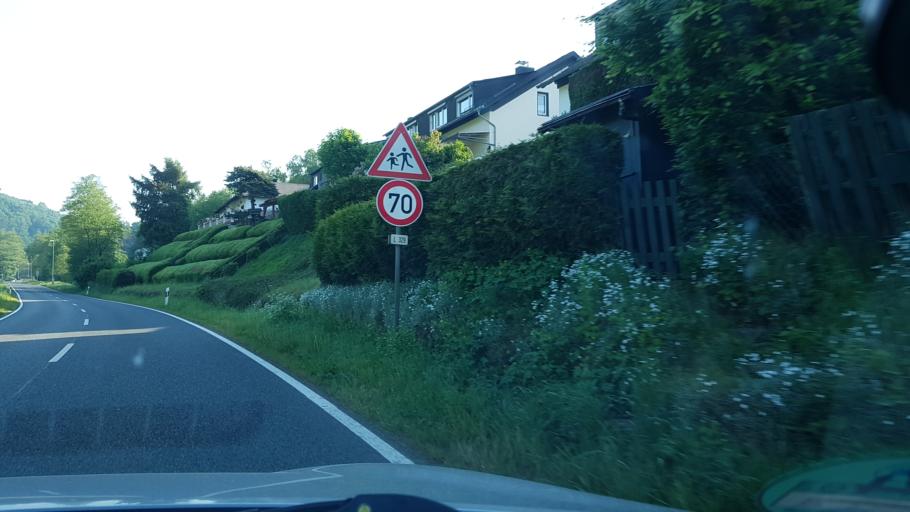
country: DE
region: Rheinland-Pfalz
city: Eitelborn
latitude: 50.3542
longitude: 7.7240
